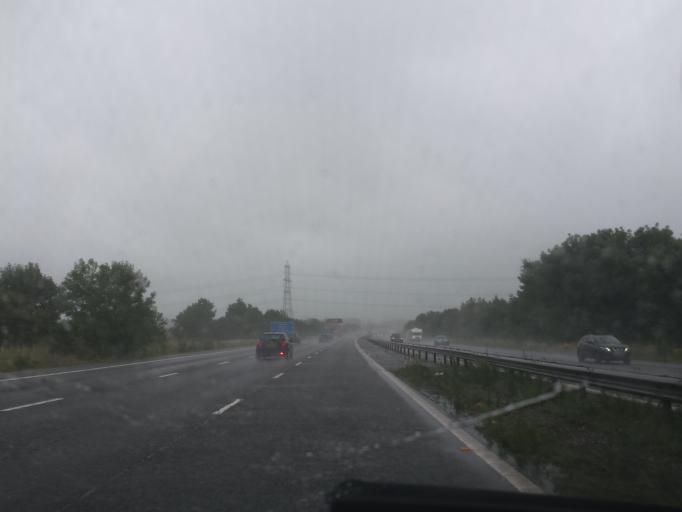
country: GB
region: England
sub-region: Leicestershire
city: Kirby Muxloe
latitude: 52.6479
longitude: -1.2314
